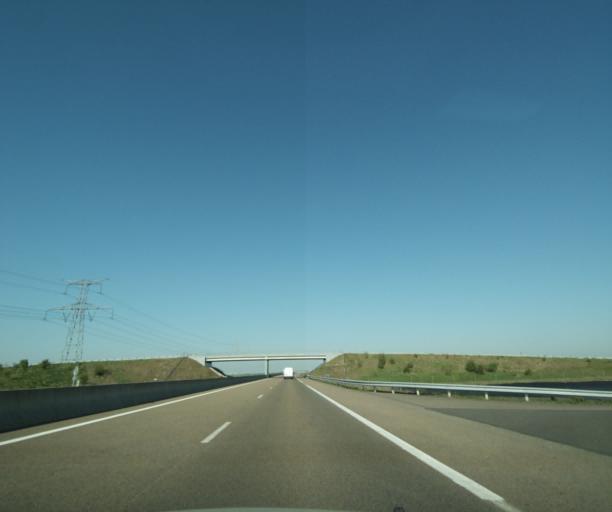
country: FR
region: Centre
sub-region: Departement du Loiret
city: Boynes
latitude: 48.0971
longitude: 2.3681
